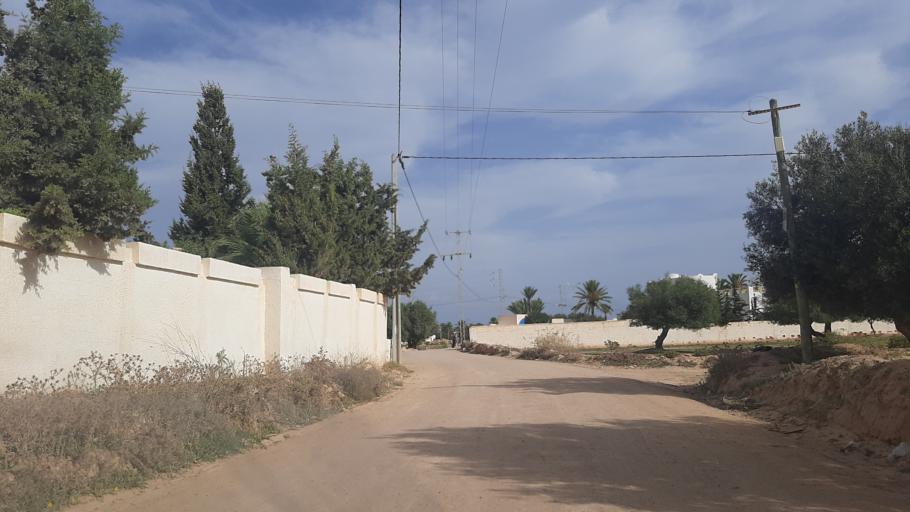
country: TN
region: Madanin
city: Midoun
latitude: 33.8170
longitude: 11.0257
